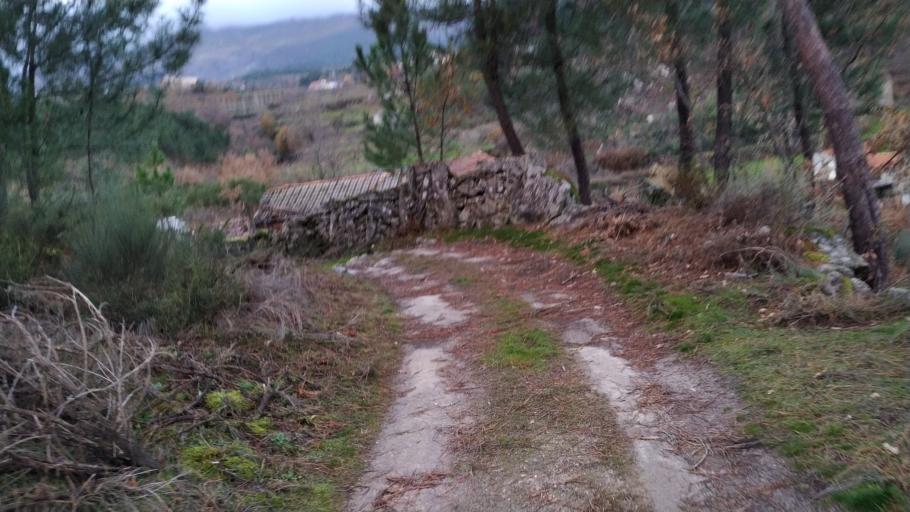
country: PT
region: Vila Real
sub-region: Vila Real
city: Vila Real
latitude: 41.3525
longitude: -7.7145
